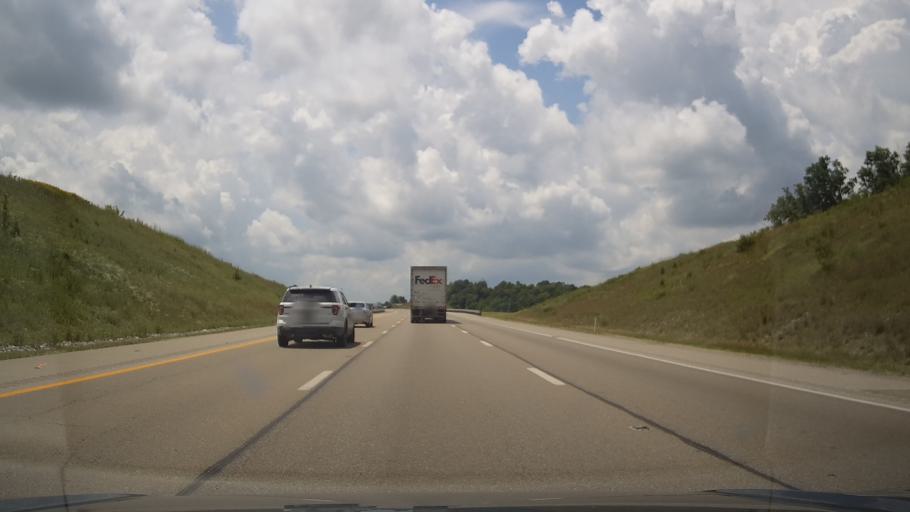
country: US
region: Kentucky
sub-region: Grant County
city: Williamstown
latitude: 38.5829
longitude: -84.5886
